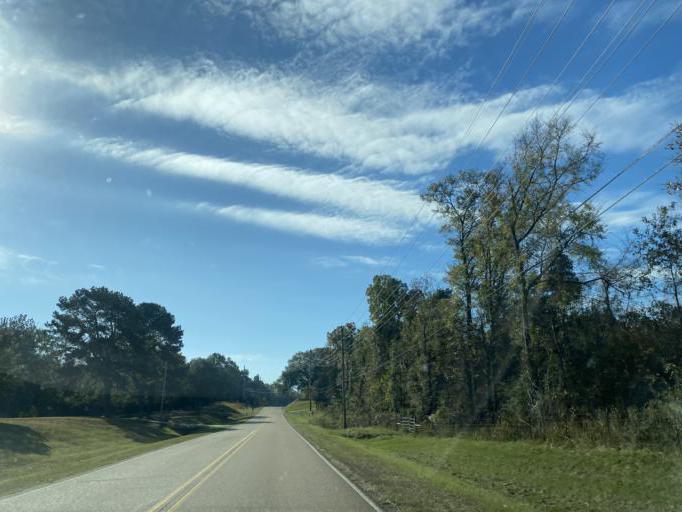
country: US
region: Mississippi
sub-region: Madison County
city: Madison
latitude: 32.4784
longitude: -90.1788
